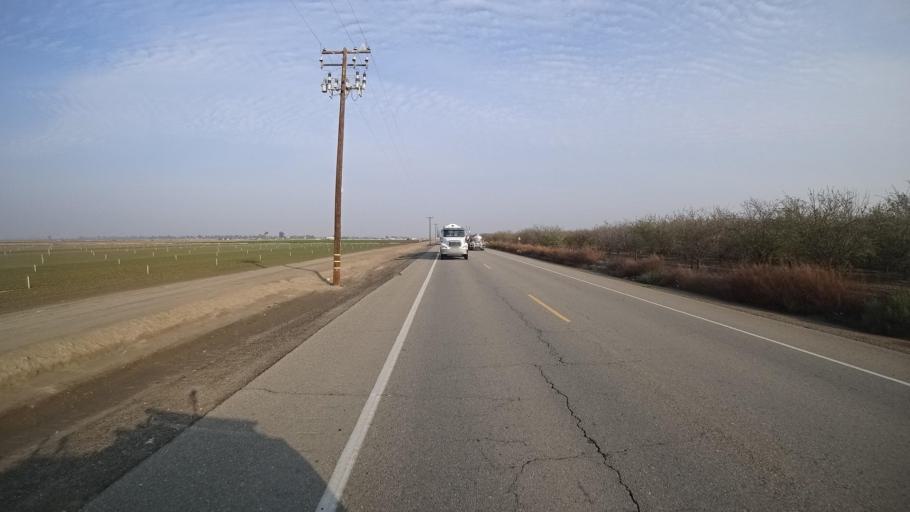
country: US
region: California
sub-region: Kern County
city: Weedpatch
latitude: 35.1603
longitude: -118.9147
